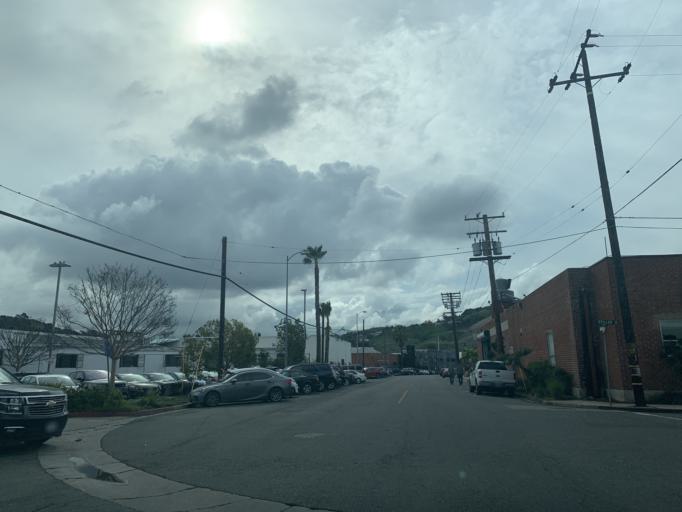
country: US
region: California
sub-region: Los Angeles County
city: Culver City
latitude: 34.0247
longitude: -118.3780
